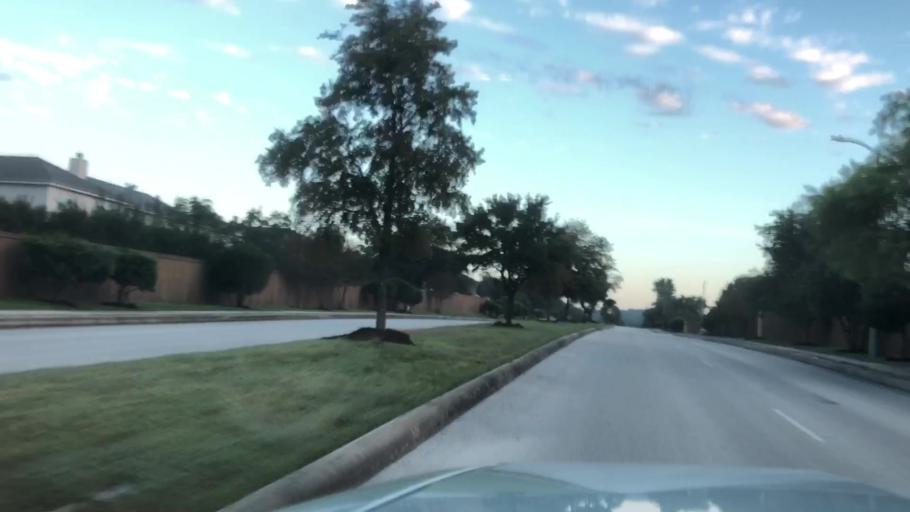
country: US
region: Texas
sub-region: Bexar County
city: Helotes
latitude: 29.5467
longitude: -98.6464
